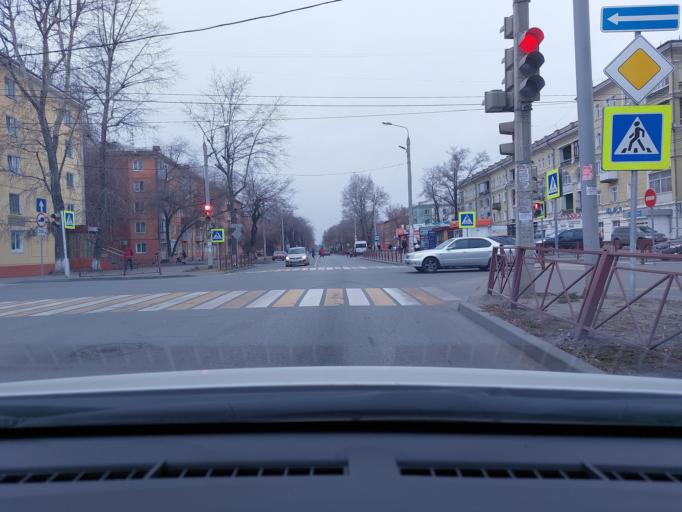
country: RU
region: Irkutsk
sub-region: Irkutskiy Rayon
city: Irkutsk
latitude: 52.3454
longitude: 104.2257
